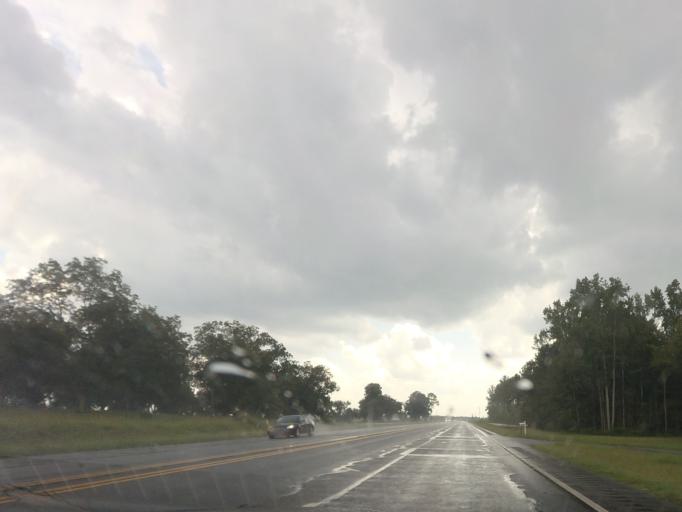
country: US
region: Georgia
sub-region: Bleckley County
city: Cochran
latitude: 32.4491
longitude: -83.3802
